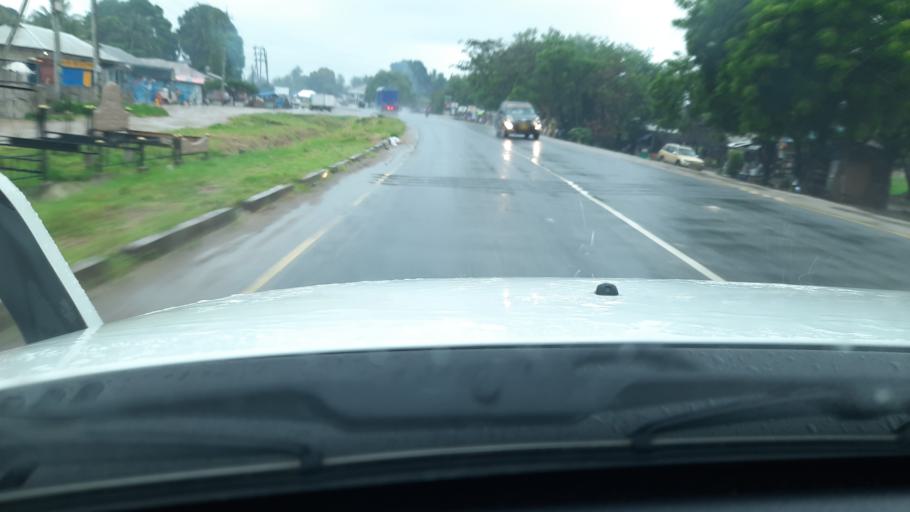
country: TZ
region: Pwani
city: Bagamoyo
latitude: -6.5925
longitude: 39.0607
